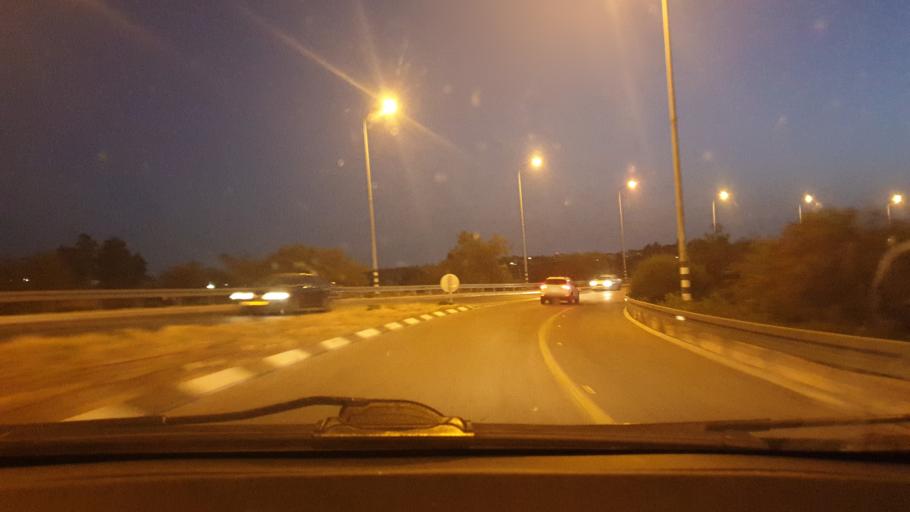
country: IL
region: Central District
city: Bene 'Ayish
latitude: 31.7930
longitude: 34.7685
